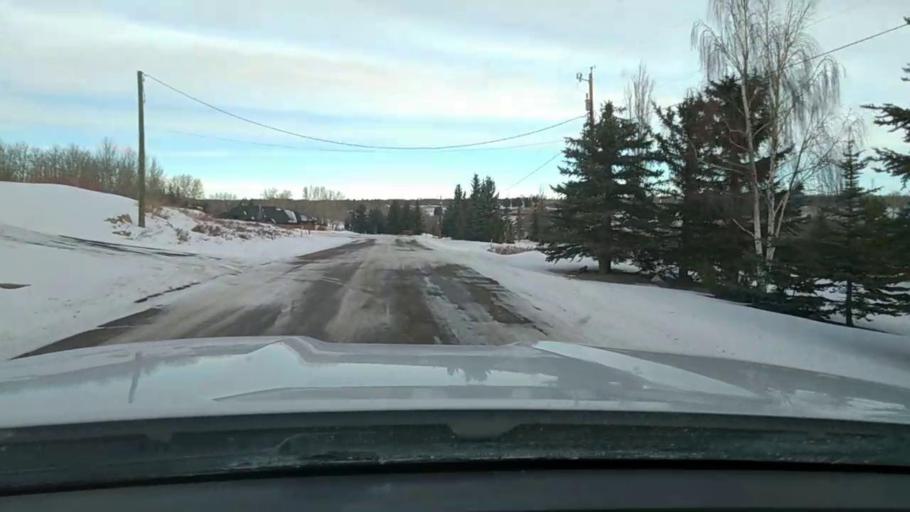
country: CA
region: Alberta
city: Cochrane
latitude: 51.1518
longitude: -114.2697
